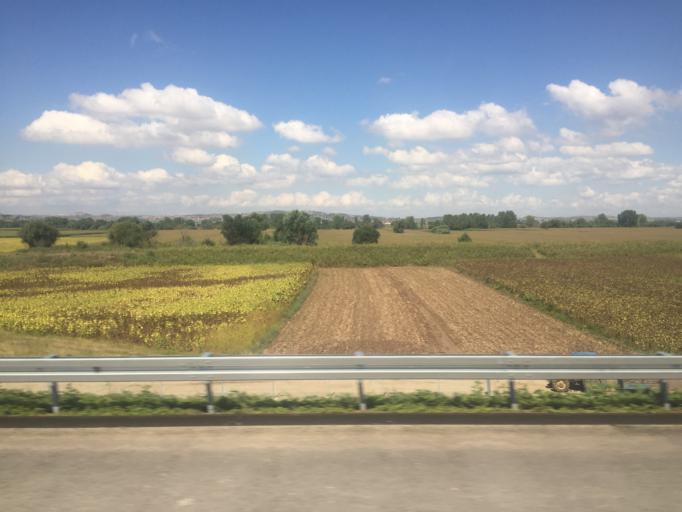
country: TR
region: Balikesir
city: Gobel
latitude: 40.0129
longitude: 28.1990
